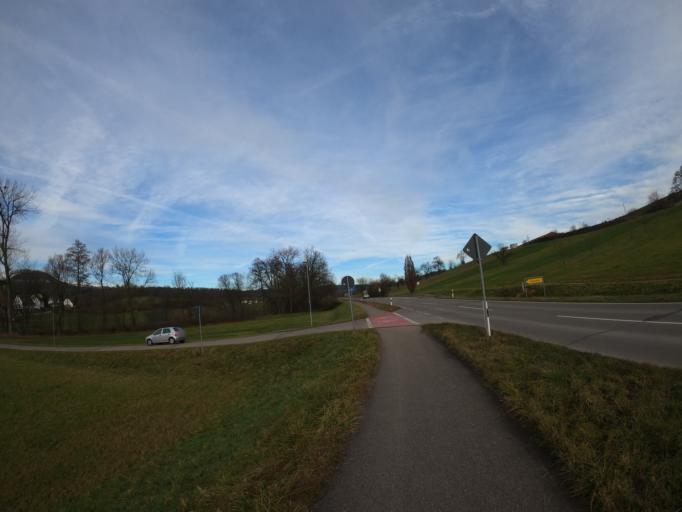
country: DE
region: Baden-Wuerttemberg
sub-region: Regierungsbezirk Stuttgart
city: Ottenbach
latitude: 48.7204
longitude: 9.7373
